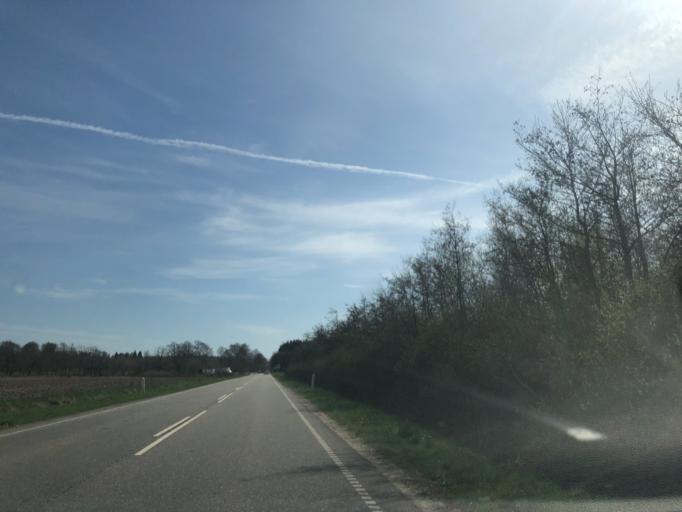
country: DK
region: Zealand
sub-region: Faxe Kommune
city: Haslev
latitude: 55.3430
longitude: 11.9409
